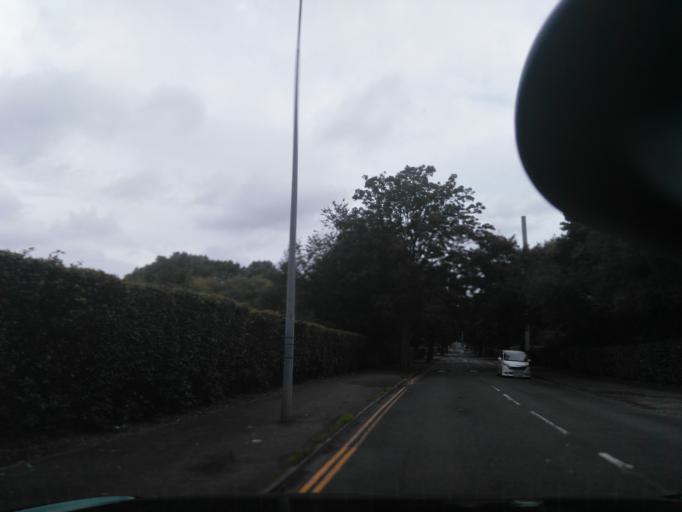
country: GB
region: England
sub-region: Borough of Swindon
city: Swindon
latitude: 51.5757
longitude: -1.7864
